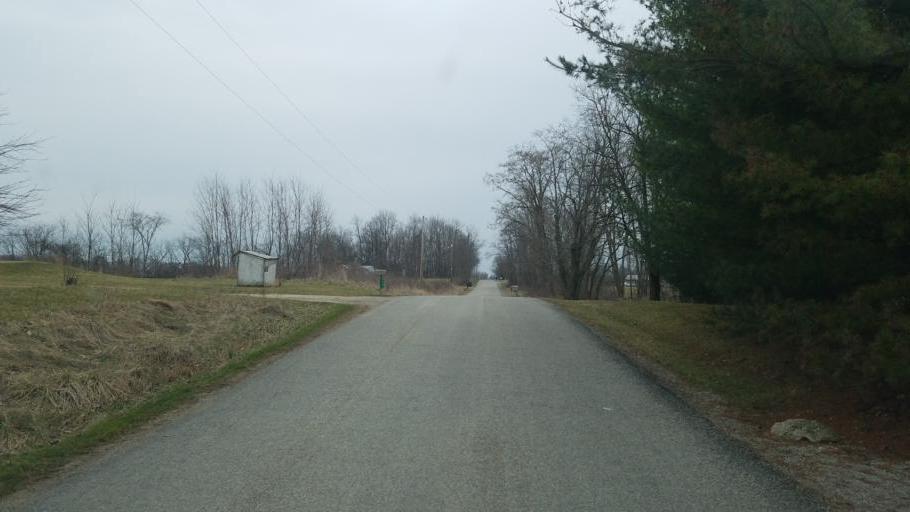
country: US
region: Ohio
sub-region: Morrow County
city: Mount Gilead
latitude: 40.6367
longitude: -82.7959
